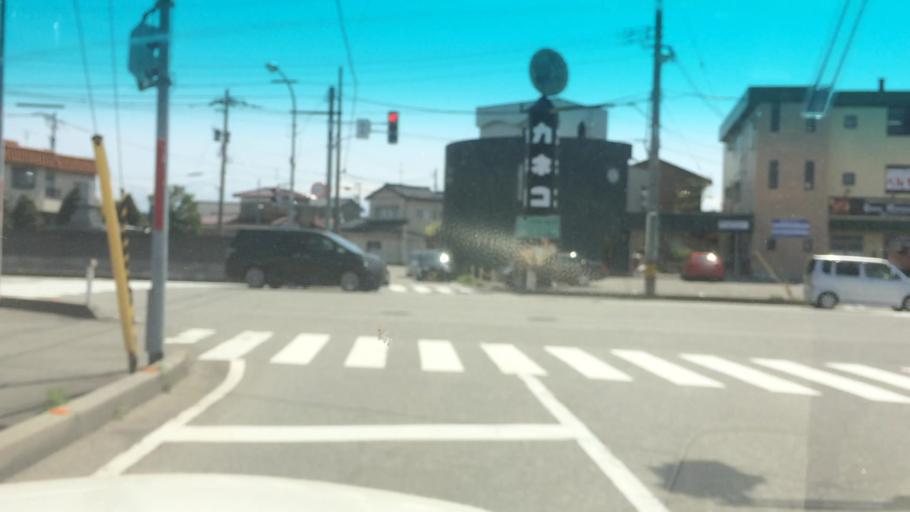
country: JP
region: Toyama
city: Toyama-shi
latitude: 36.6778
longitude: 137.2492
